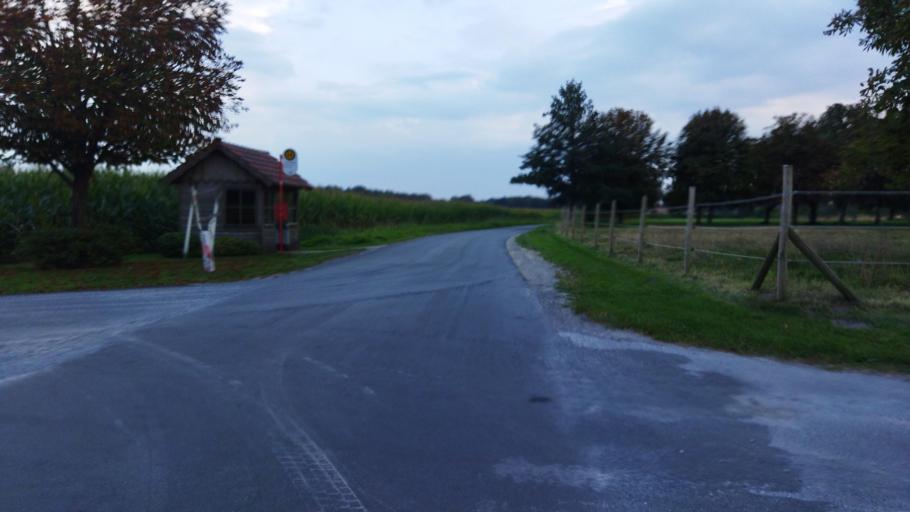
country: DE
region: Lower Saxony
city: Bad Iburg
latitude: 52.1293
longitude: 8.0572
